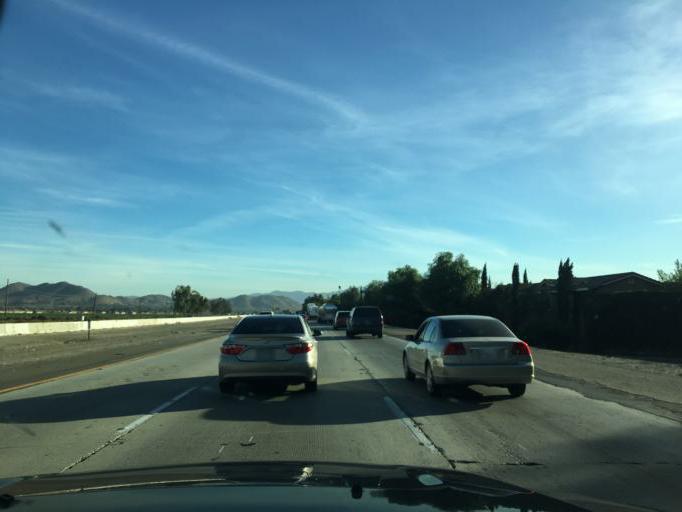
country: US
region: California
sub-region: Riverside County
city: Mira Loma
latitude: 33.9911
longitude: -117.5503
